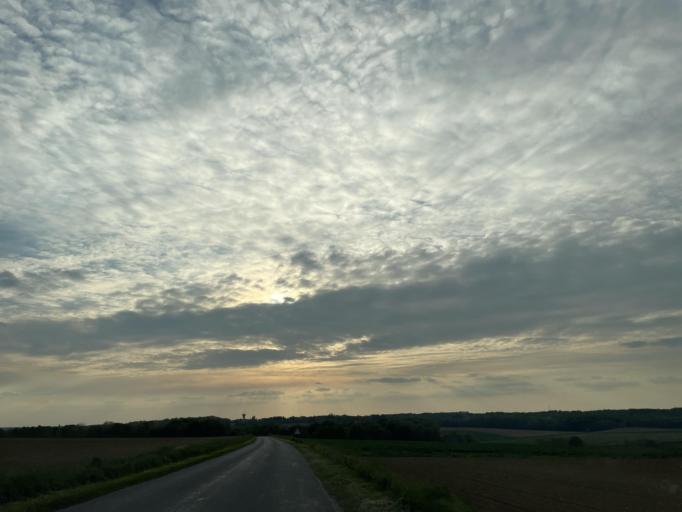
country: FR
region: Ile-de-France
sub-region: Departement de Seine-et-Marne
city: Bouleurs
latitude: 48.8936
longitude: 2.9166
